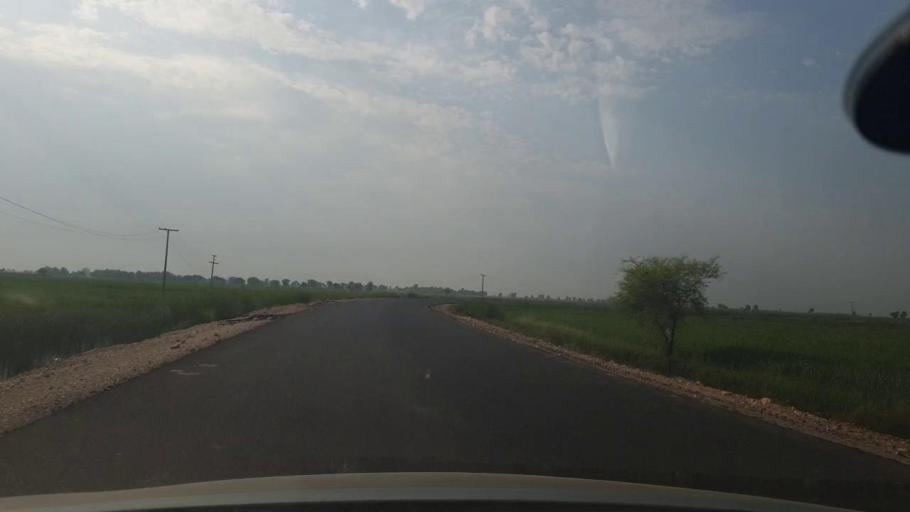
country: PK
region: Sindh
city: Jacobabad
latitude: 28.0971
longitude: 68.3295
